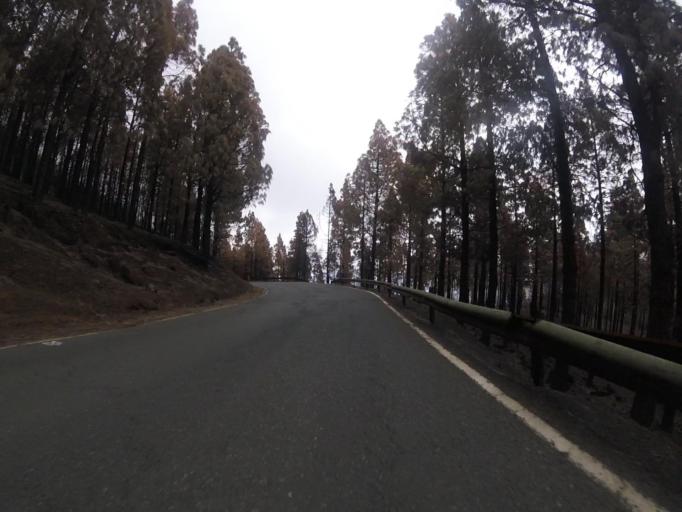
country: ES
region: Canary Islands
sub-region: Provincia de Las Palmas
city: Tejeda
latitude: 27.9817
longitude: -15.5801
